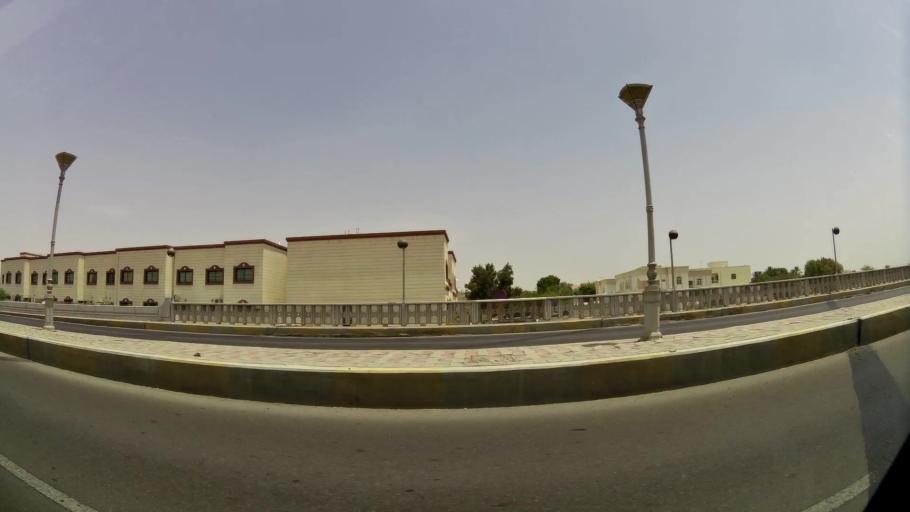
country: AE
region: Abu Dhabi
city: Al Ain
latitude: 24.2051
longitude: 55.7495
